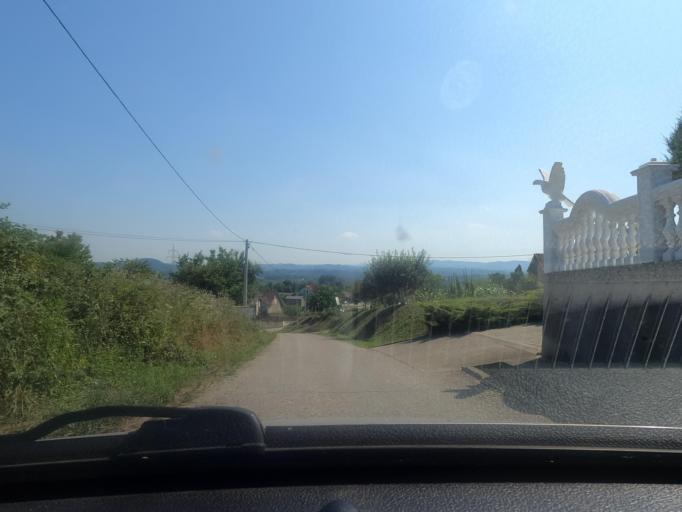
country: RS
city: Jarebice
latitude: 44.5378
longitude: 19.3762
